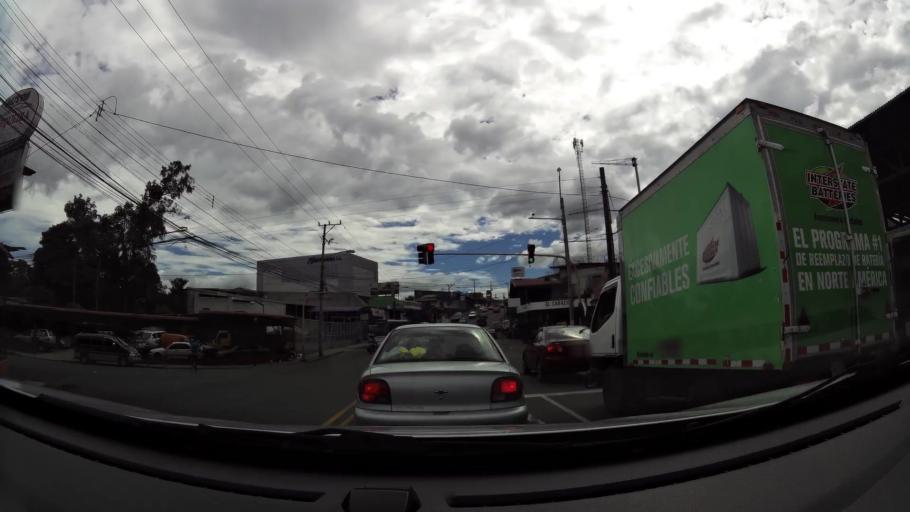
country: CR
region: San Jose
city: San Jose
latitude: 9.9169
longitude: -84.0844
